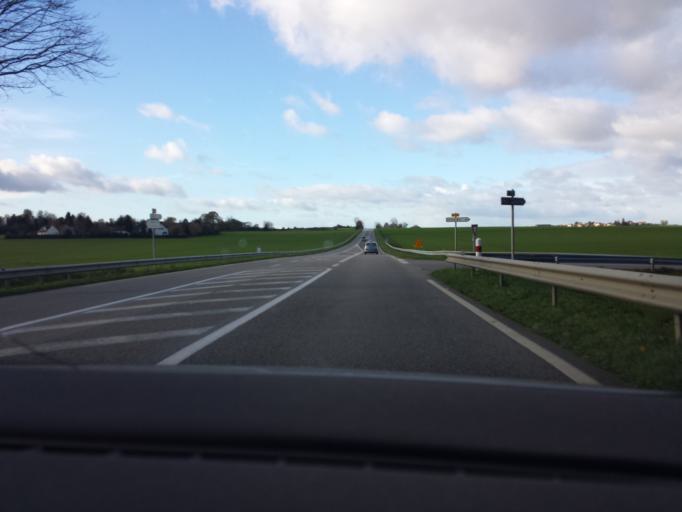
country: FR
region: Haute-Normandie
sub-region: Departement de l'Eure
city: Breuilpont
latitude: 49.0162
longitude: 1.4615
